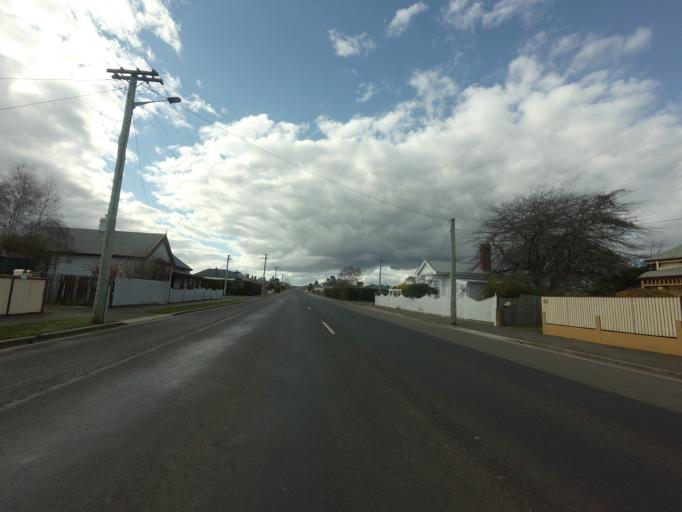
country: AU
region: Tasmania
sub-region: Northern Midlands
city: Longford
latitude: -41.6003
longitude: 147.1203
